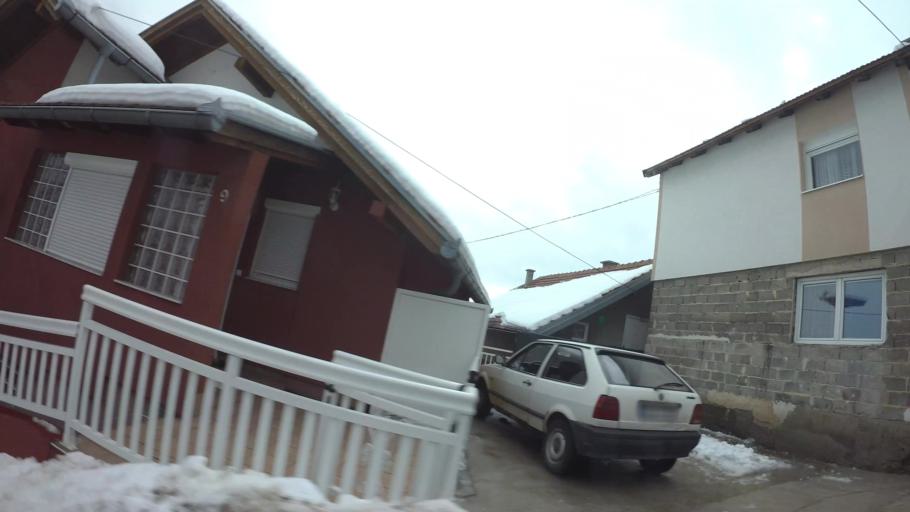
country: BA
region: Federation of Bosnia and Herzegovina
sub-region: Kanton Sarajevo
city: Sarajevo
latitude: 43.8602
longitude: 18.3419
